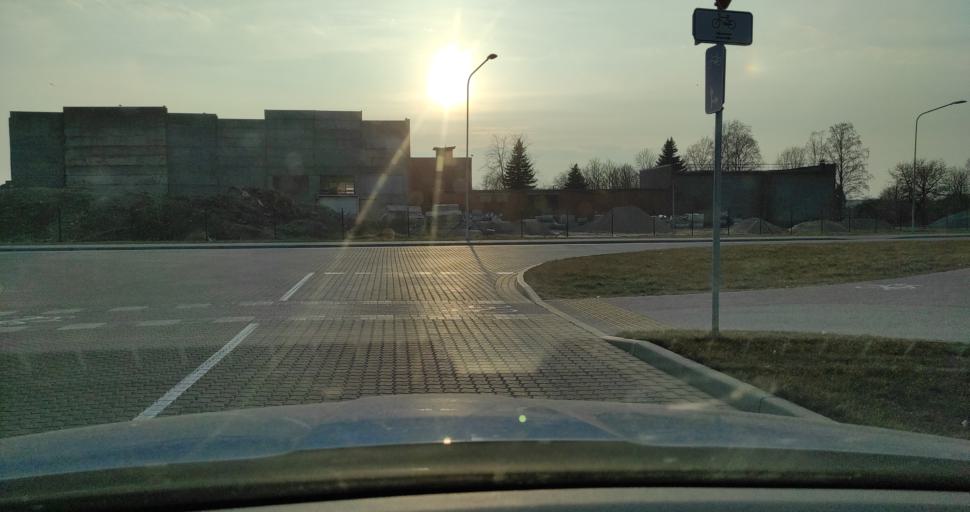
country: LV
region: Ventspils
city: Ventspils
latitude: 57.3852
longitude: 21.5819
